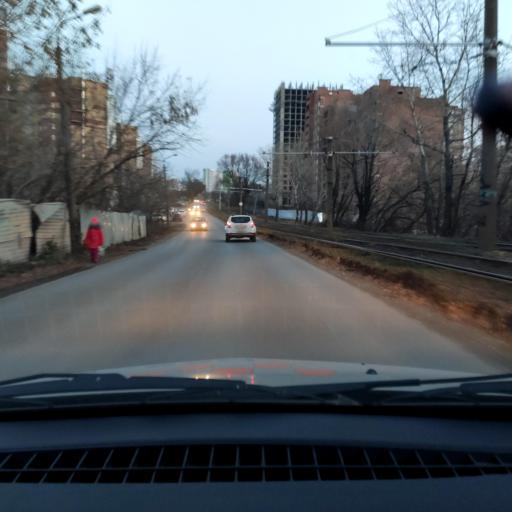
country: RU
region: Bashkortostan
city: Ufa
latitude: 54.7159
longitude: 55.9728
